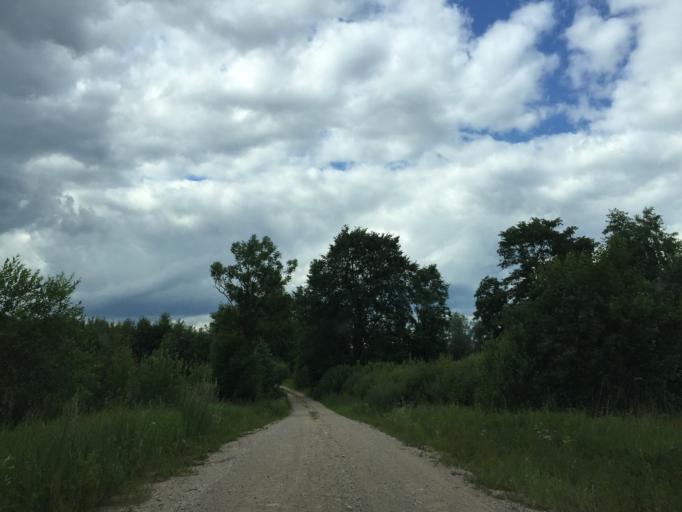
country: LV
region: Ogre
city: Jumprava
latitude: 56.8431
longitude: 25.0522
